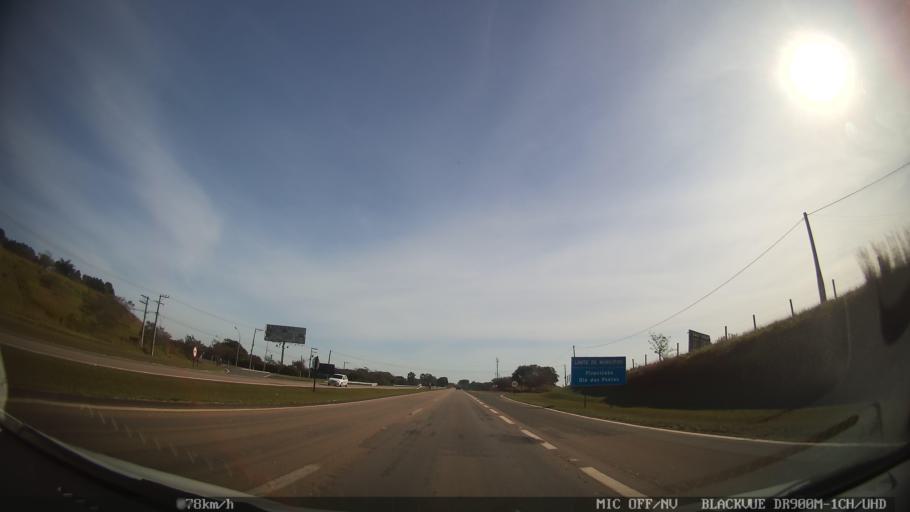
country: BR
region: Sao Paulo
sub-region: Rio Das Pedras
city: Rio das Pedras
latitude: -22.7794
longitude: -47.5890
